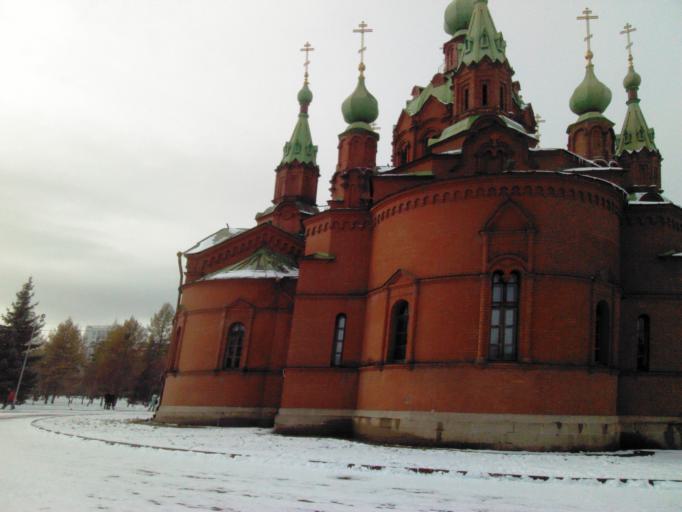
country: RU
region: Chelyabinsk
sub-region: Gorod Chelyabinsk
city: Chelyabinsk
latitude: 55.1626
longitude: 61.3917
